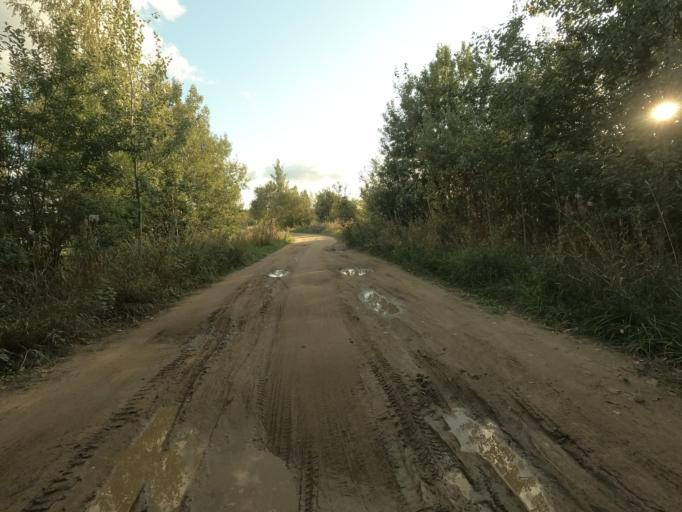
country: RU
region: Leningrad
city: Otradnoye
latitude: 59.8583
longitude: 30.7978
